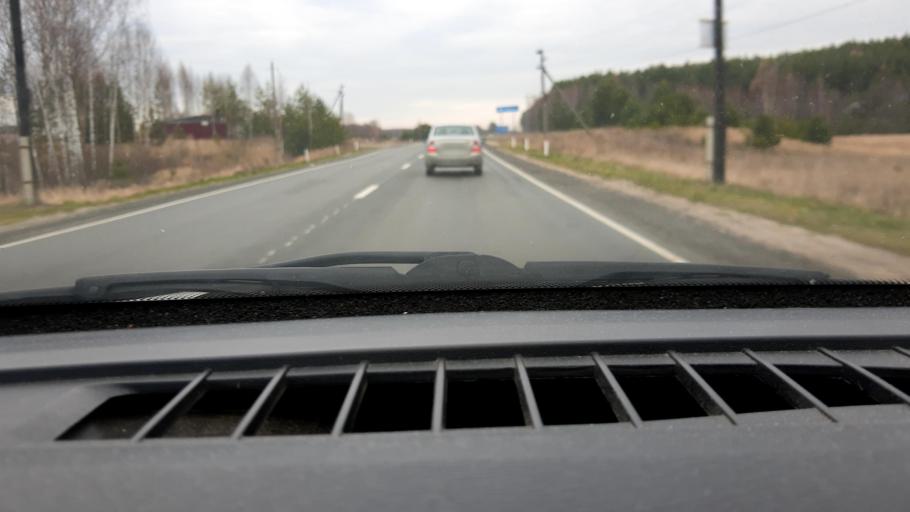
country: RU
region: Nizjnij Novgorod
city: Novaya Balakhna
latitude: 56.6114
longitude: 43.6005
